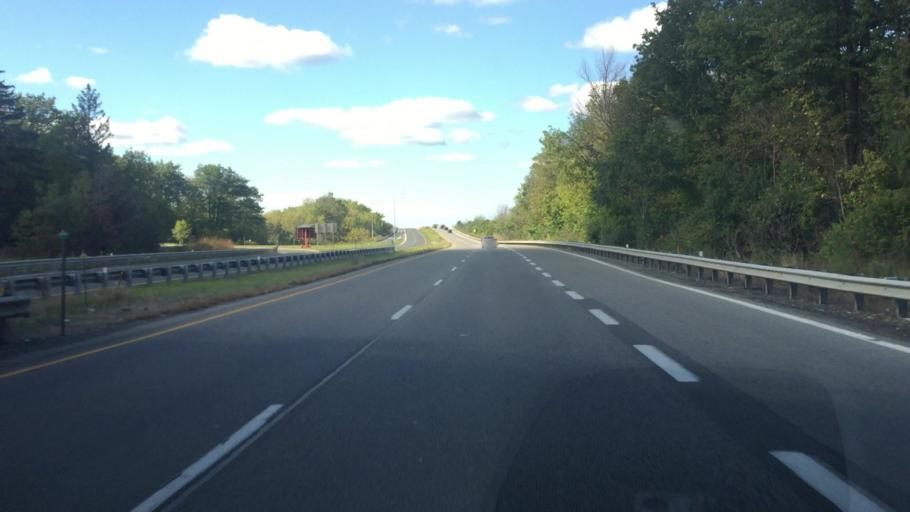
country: CA
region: Ontario
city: Fort Erie
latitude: 42.9336
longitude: -78.9834
